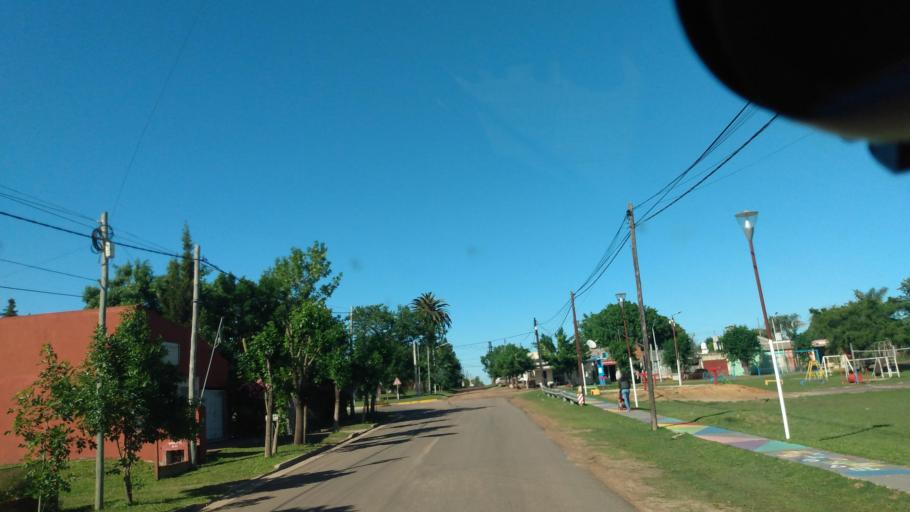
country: AR
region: Entre Rios
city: Colon
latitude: -32.1571
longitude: -58.1977
